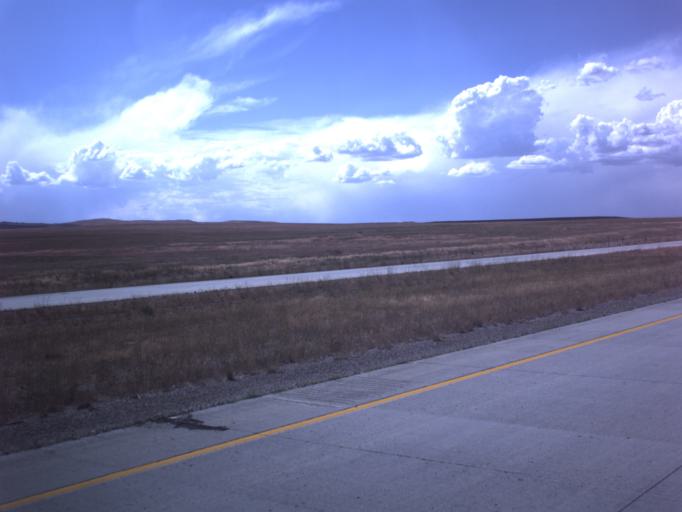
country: US
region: Utah
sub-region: Box Elder County
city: Garland
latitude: 41.8662
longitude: -112.4598
